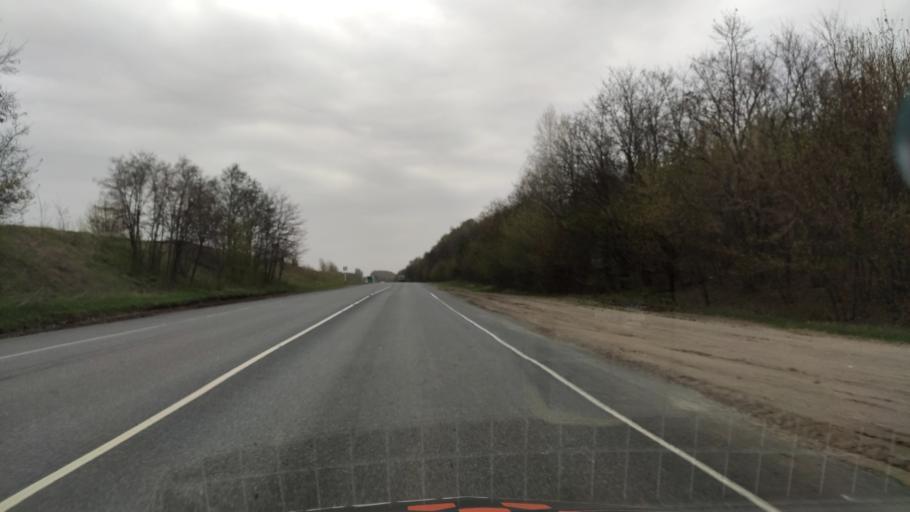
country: RU
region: Kursk
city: Gorshechnoye
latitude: 51.4697
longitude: 37.9365
